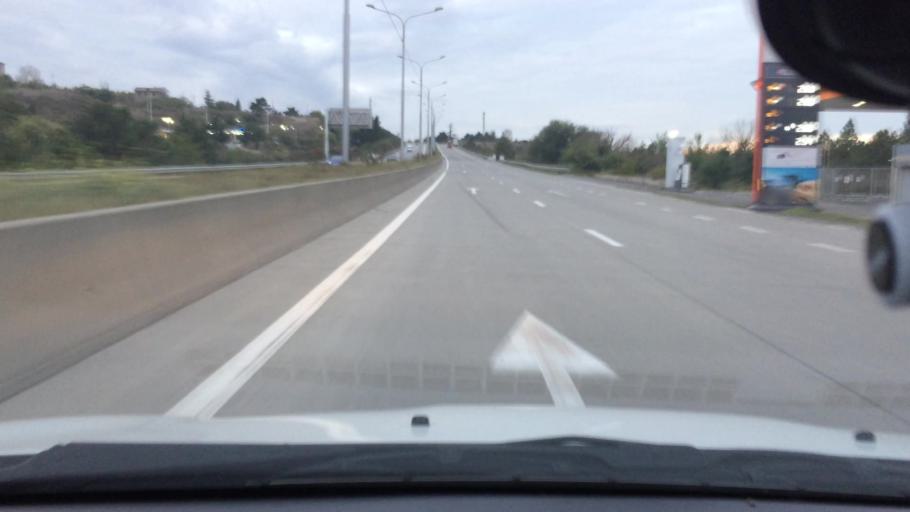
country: GE
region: Mtskheta-Mtianeti
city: Mtskheta
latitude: 41.8941
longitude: 44.7114
